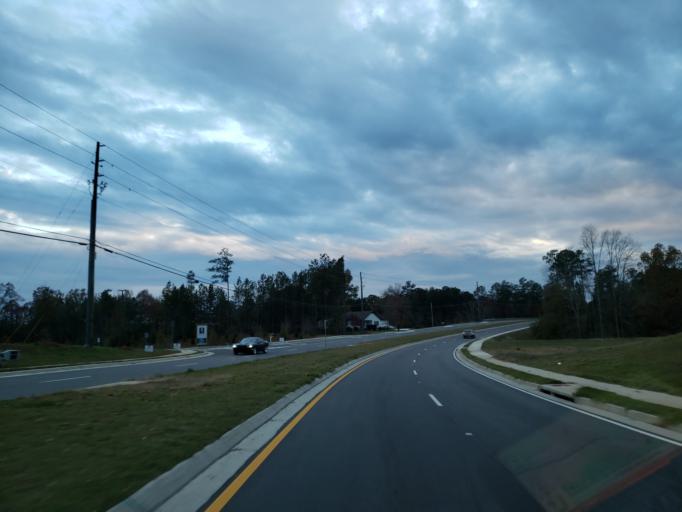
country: US
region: Georgia
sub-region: Cobb County
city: Acworth
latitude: 34.0579
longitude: -84.7336
